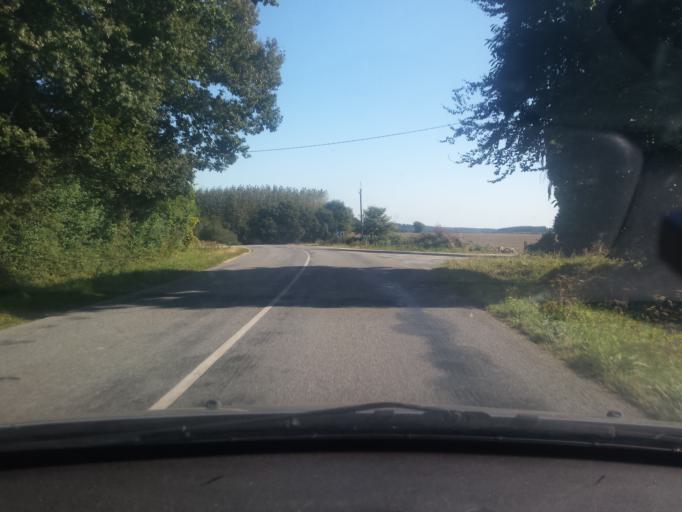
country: FR
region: Brittany
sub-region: Departement du Morbihan
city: Cleguerec
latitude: 48.1031
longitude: -3.1072
